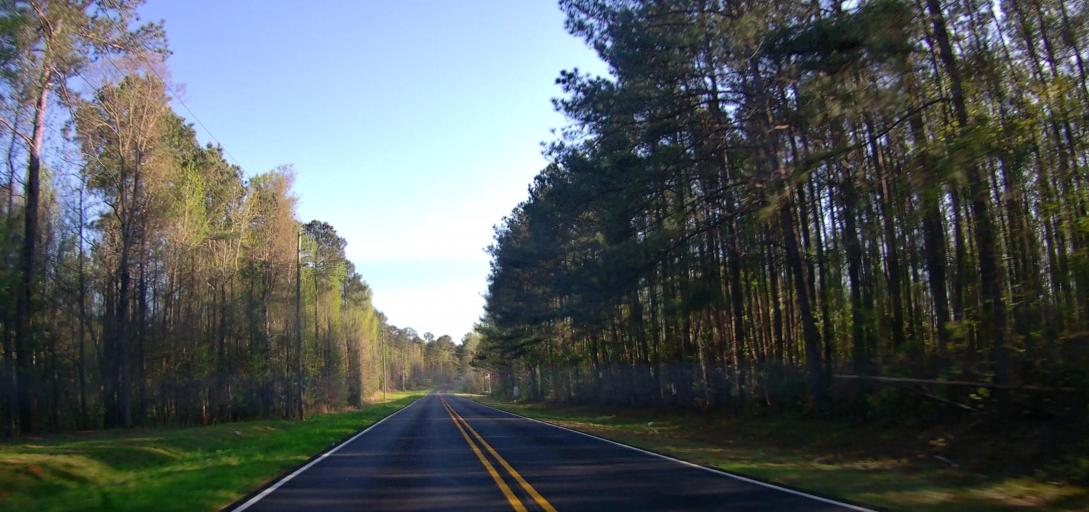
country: US
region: Georgia
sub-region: Butts County
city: Jackson
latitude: 33.3622
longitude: -83.9095
